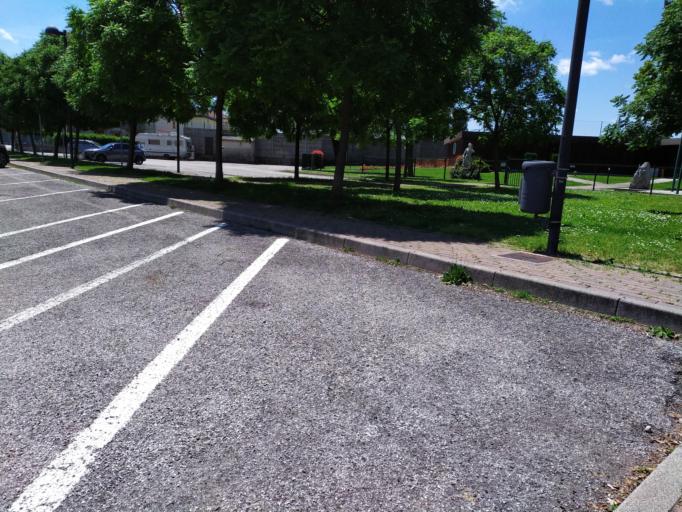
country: IT
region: Veneto
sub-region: Provincia di Vicenza
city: Tavernelle
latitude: 45.4998
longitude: 11.4423
